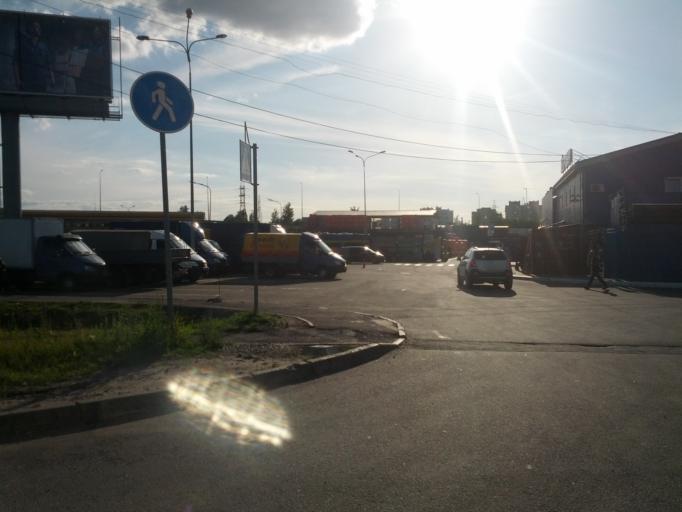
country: RU
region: Leningrad
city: Rybatskoye
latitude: 59.8890
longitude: 30.5081
